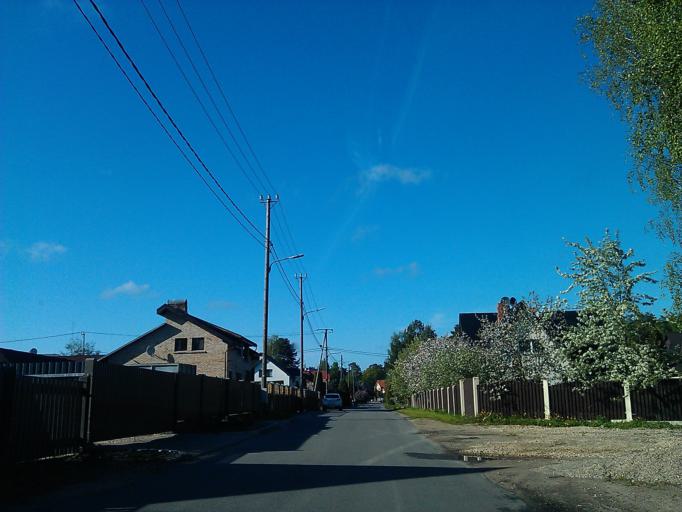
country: LV
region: Riga
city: Bergi
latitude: 57.0115
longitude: 24.2691
